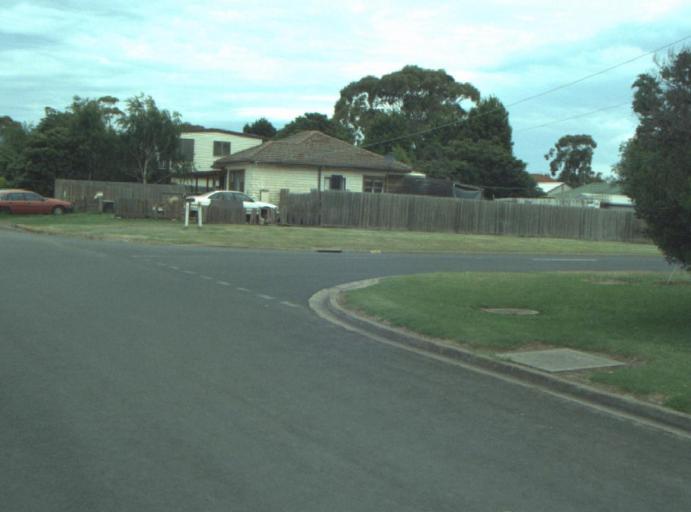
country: AU
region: Victoria
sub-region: Greater Geelong
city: Clifton Springs
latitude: -38.1168
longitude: 144.6698
